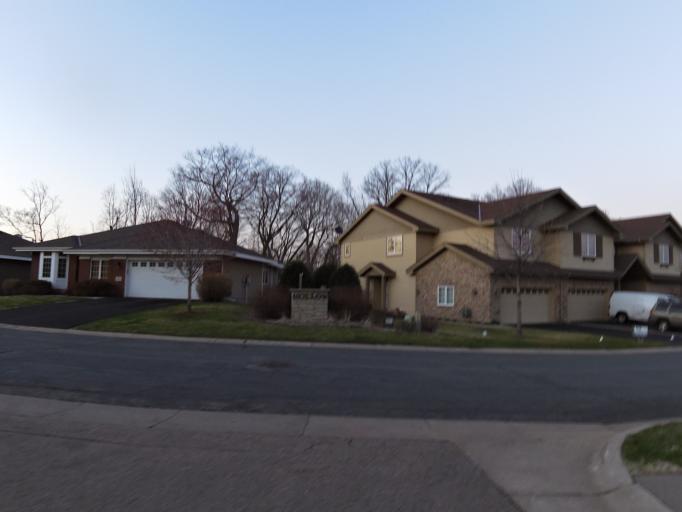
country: US
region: Minnesota
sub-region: Scott County
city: Prior Lake
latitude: 44.7309
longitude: -93.4432
